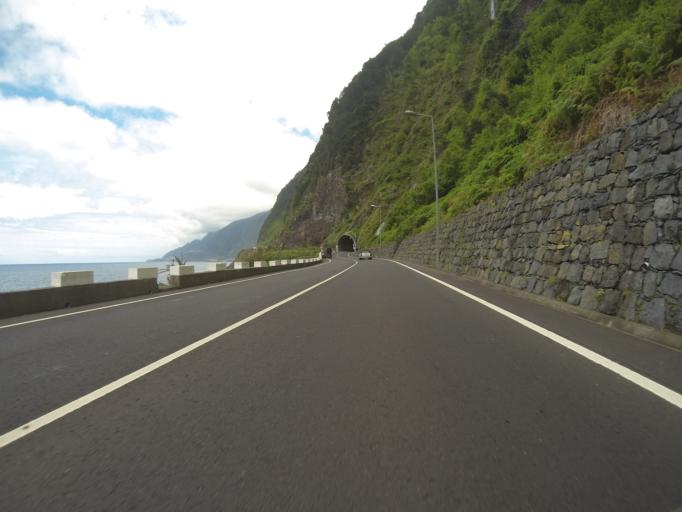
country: PT
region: Madeira
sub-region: Sao Vicente
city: Sao Vicente
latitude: 32.8145
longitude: -17.0785
